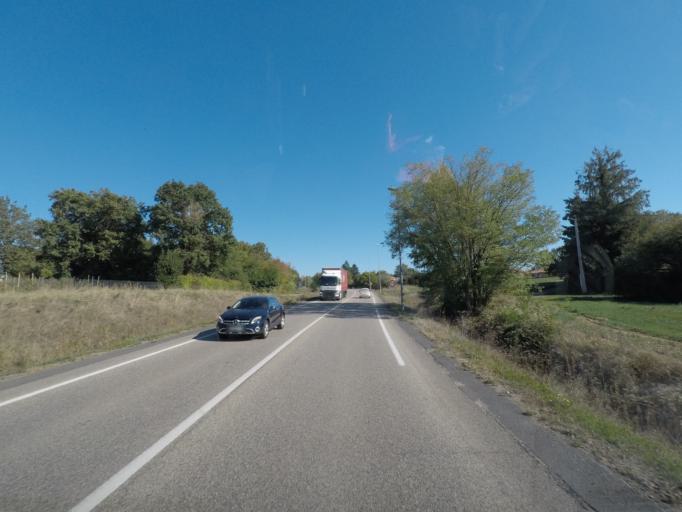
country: FR
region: Rhone-Alpes
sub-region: Departement de l'Ain
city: Peronnas
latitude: 46.1890
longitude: 5.1949
